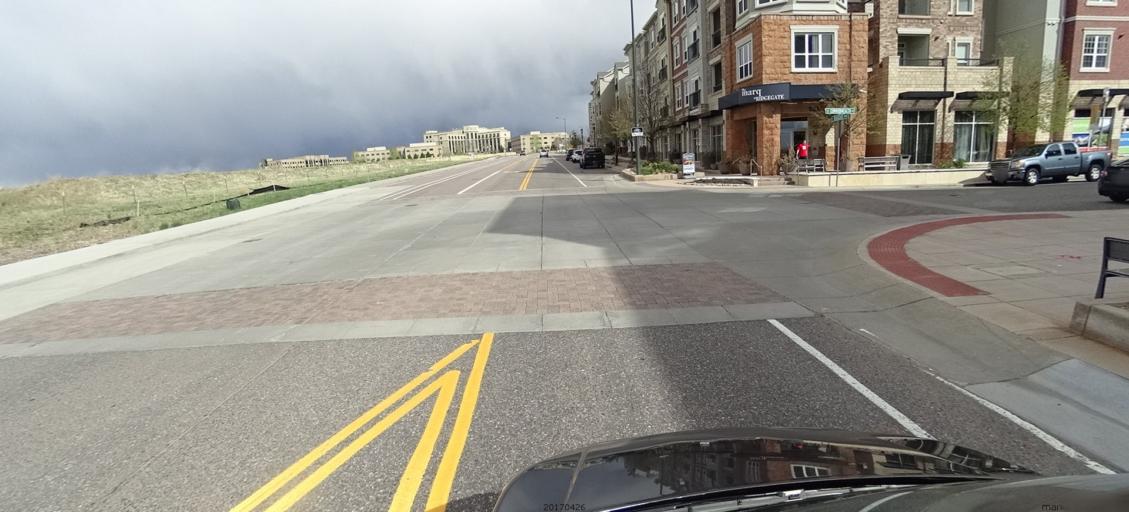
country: US
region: Colorado
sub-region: Adams County
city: Lone Tree
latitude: 39.5304
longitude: -104.8776
